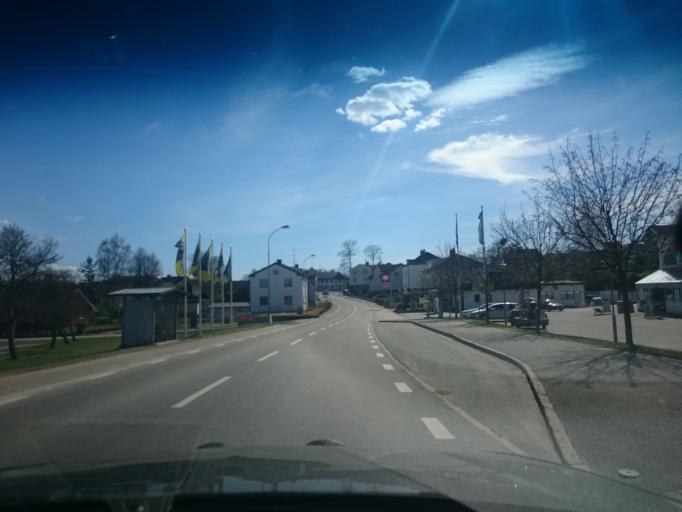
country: SE
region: Kalmar
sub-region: Hultsfreds Kommun
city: Virserum
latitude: 57.3217
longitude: 15.5824
